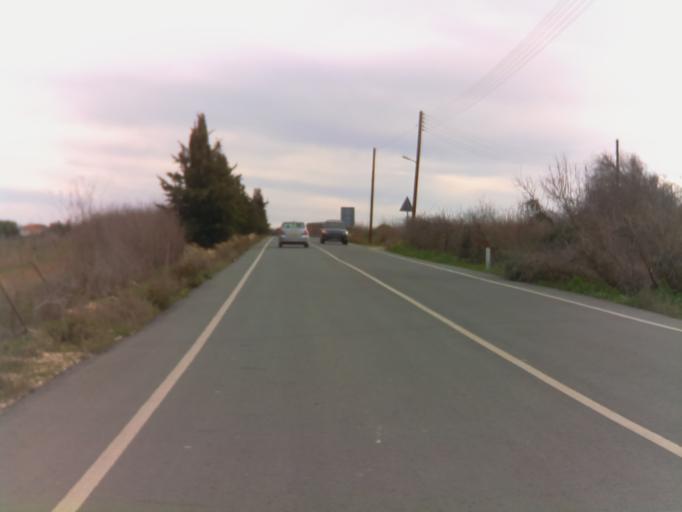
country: CY
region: Pafos
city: Pegeia
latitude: 34.9226
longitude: 32.4204
